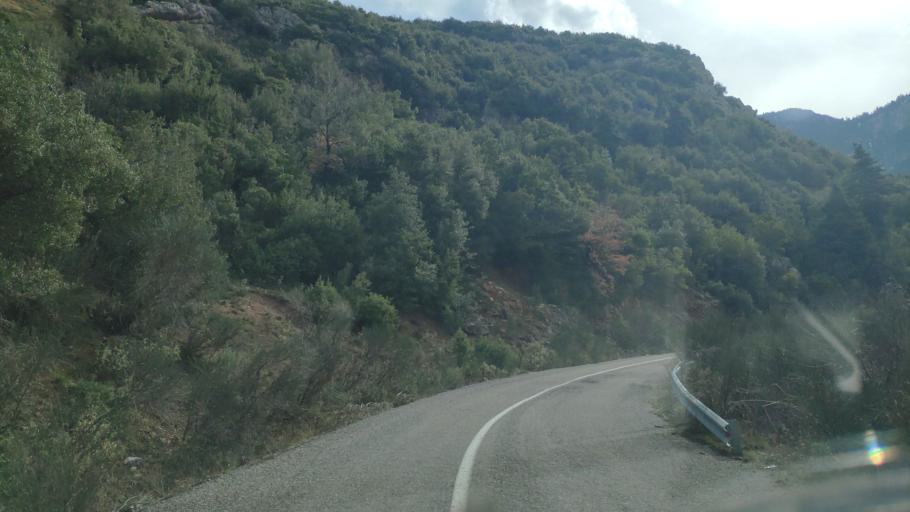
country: GR
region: Central Greece
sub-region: Nomos Fokidos
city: Amfissa
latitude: 38.6422
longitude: 22.4182
